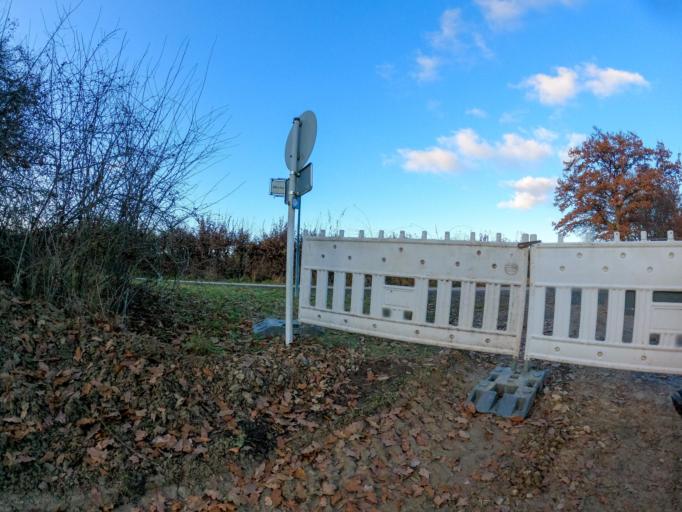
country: LU
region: Diekirch
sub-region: Canton de Wiltz
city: Bavigne
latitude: 49.9240
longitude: 5.8496
